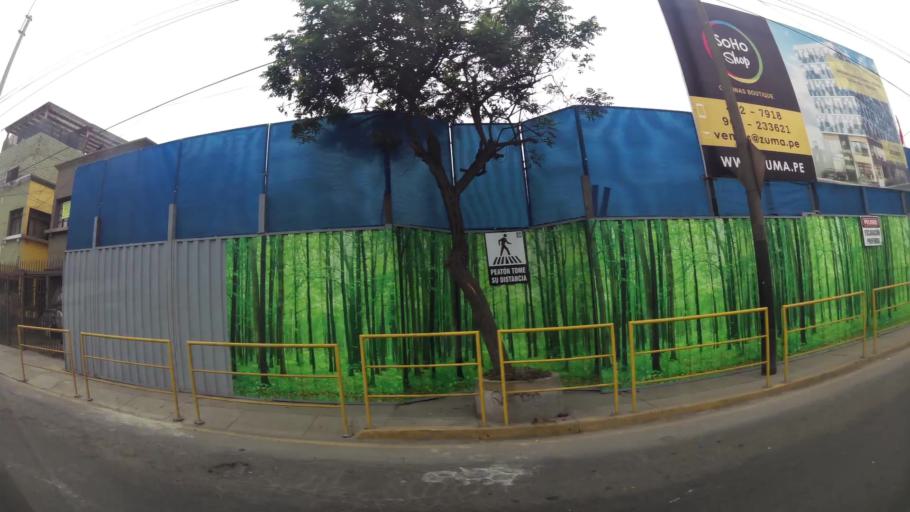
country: PE
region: Lima
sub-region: Lima
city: San Isidro
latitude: -12.1138
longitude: -77.0479
